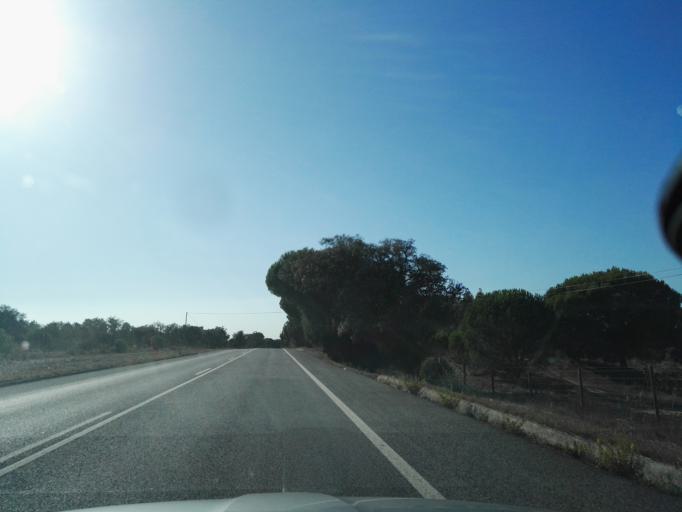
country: PT
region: Santarem
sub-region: Benavente
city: Poceirao
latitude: 38.8456
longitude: -8.7577
